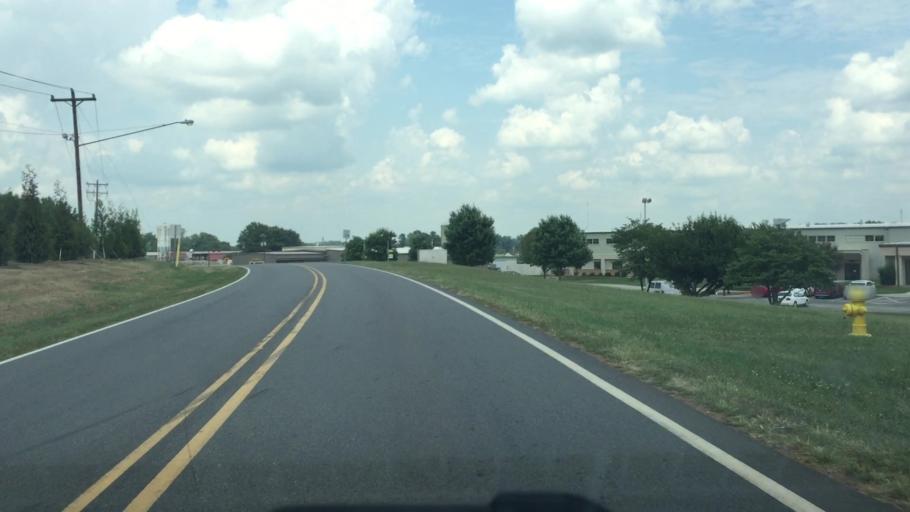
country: US
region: North Carolina
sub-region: Iredell County
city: Troutman
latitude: 35.7141
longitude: -80.8893
